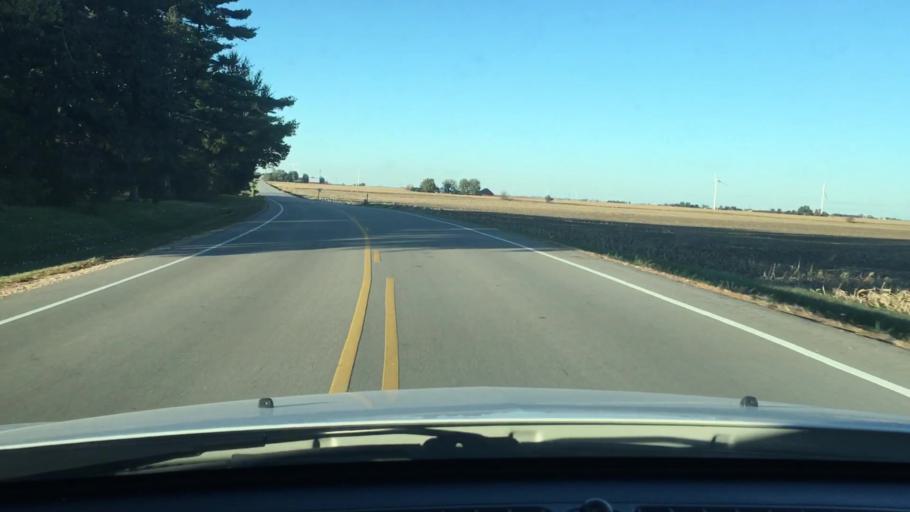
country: US
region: Illinois
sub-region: DeKalb County
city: Waterman
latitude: 41.8057
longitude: -88.8864
